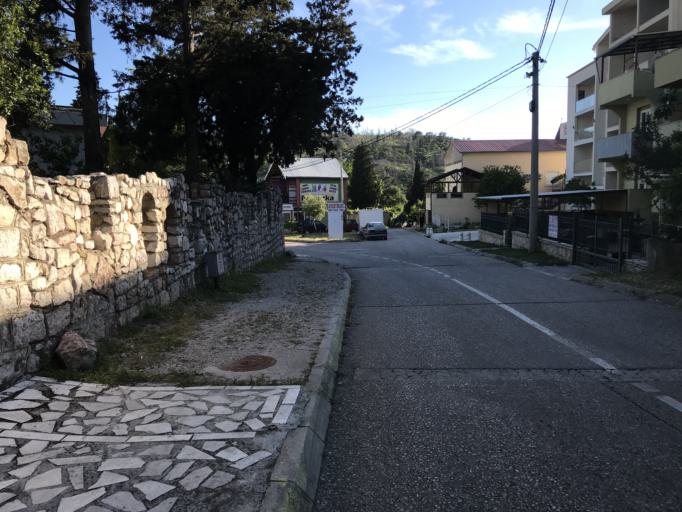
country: ME
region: Bar
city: Sutomore
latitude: 42.1417
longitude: 19.0462
